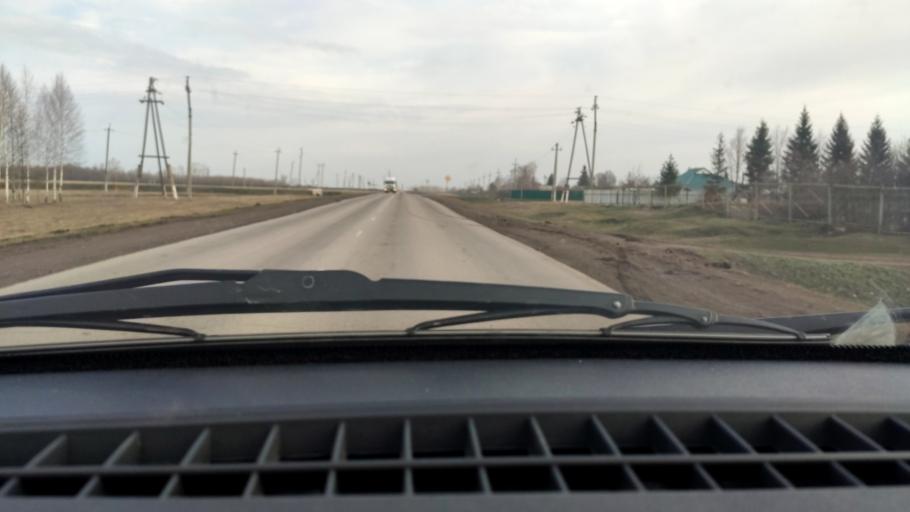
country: RU
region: Bashkortostan
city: Davlekanovo
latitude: 54.3759
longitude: 55.1956
